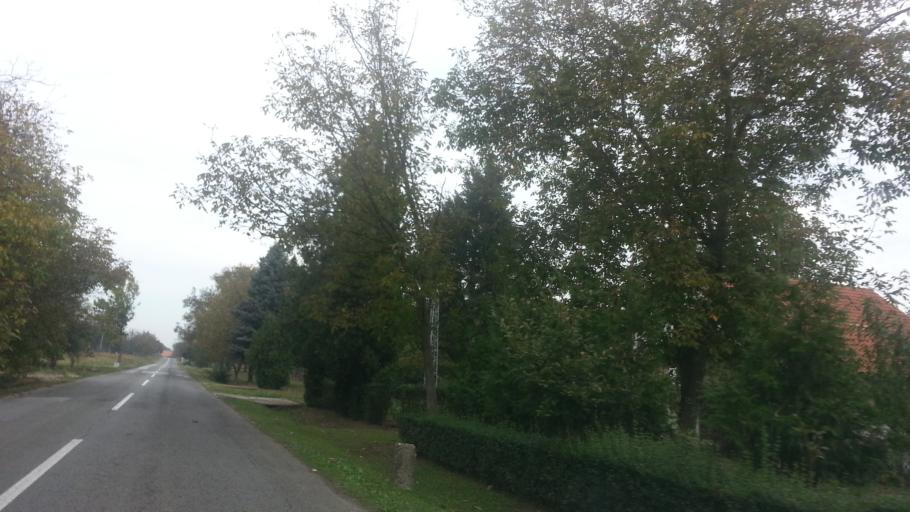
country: RS
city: Surduk
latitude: 45.0635
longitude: 20.3302
